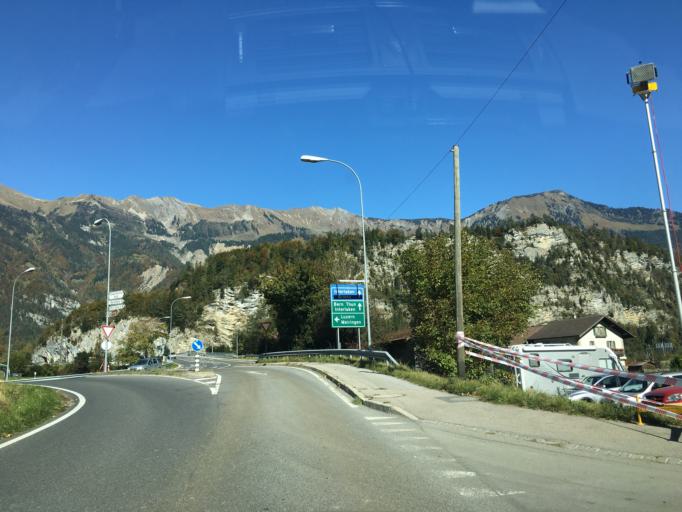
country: CH
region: Bern
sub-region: Interlaken-Oberhasli District
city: Brienz
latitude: 46.7409
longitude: 8.0596
